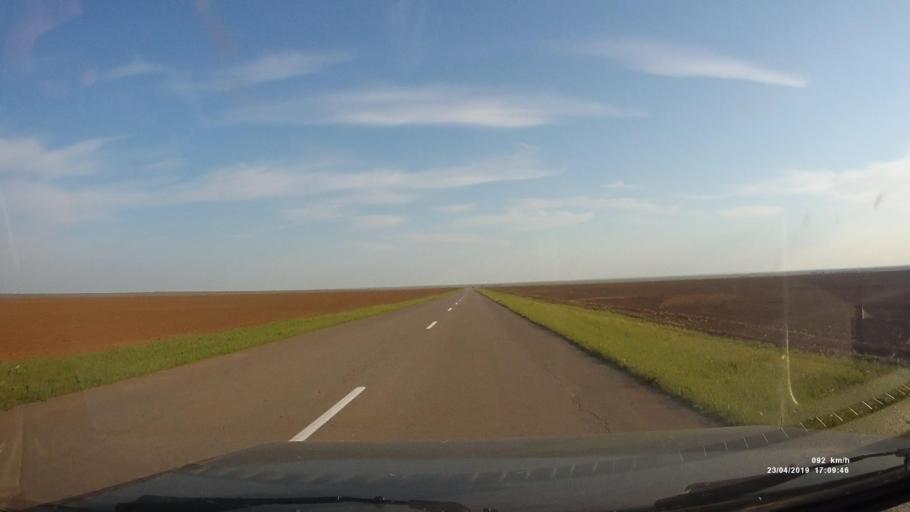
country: RU
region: Kalmykiya
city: Priyutnoye
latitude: 46.2540
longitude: 43.4842
